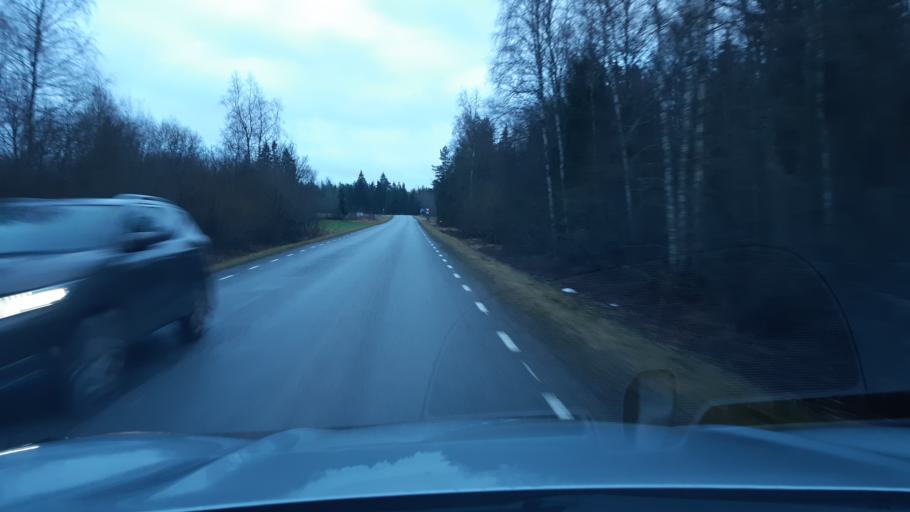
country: EE
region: Raplamaa
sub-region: Rapla vald
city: Rapla
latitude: 59.0276
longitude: 24.6800
